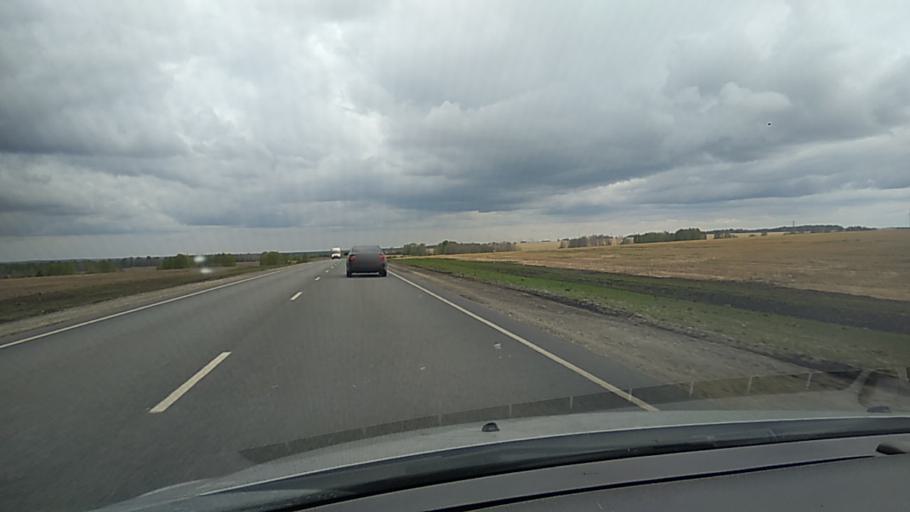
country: RU
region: Kurgan
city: Dalmatovo
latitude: 56.2891
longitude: 62.7738
